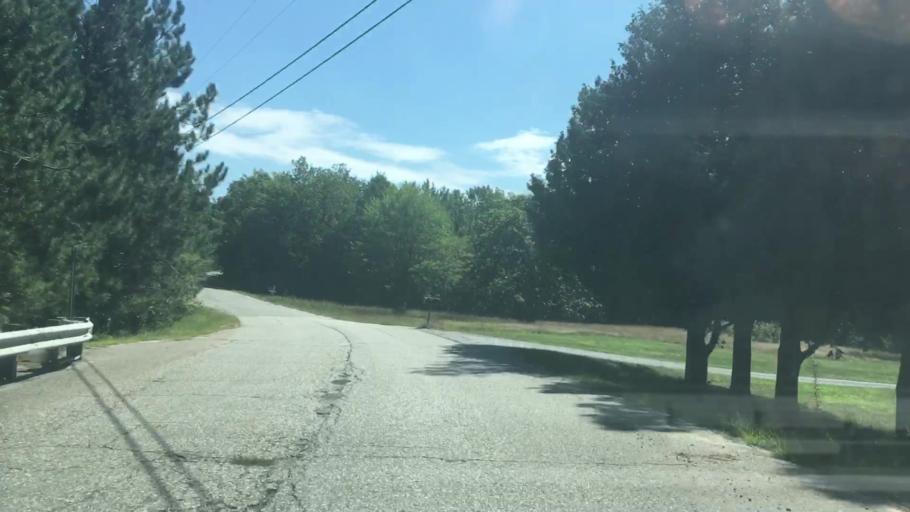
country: US
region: Maine
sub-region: Androscoggin County
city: Sabattus
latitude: 44.1230
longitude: -70.0354
